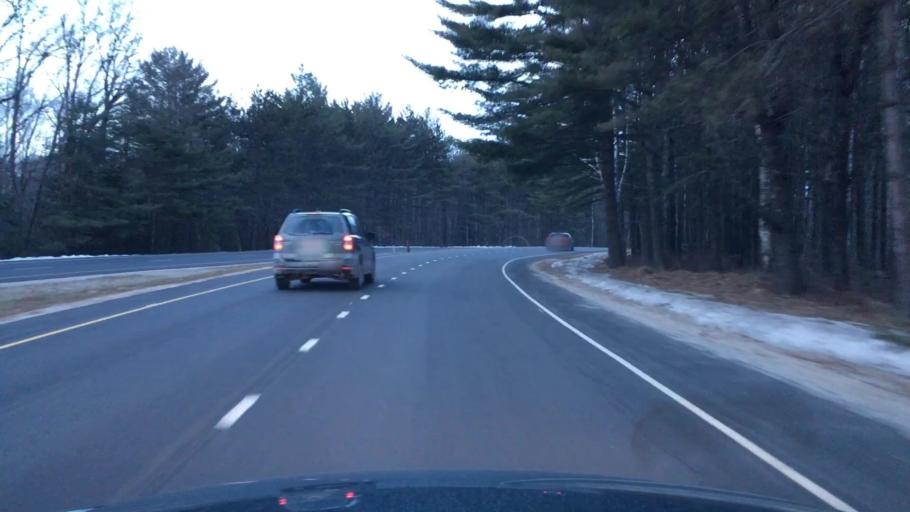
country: US
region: New Hampshire
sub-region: Merrimack County
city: Newbury
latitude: 43.3364
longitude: -72.0743
